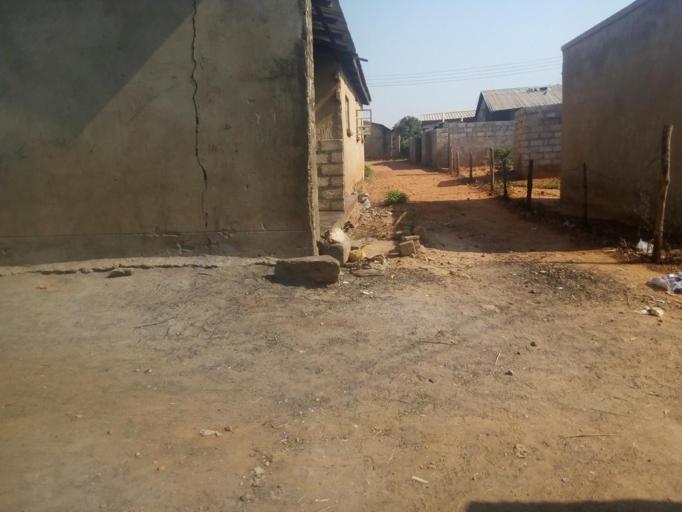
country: ZM
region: Lusaka
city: Lusaka
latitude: -15.4026
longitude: 28.3716
